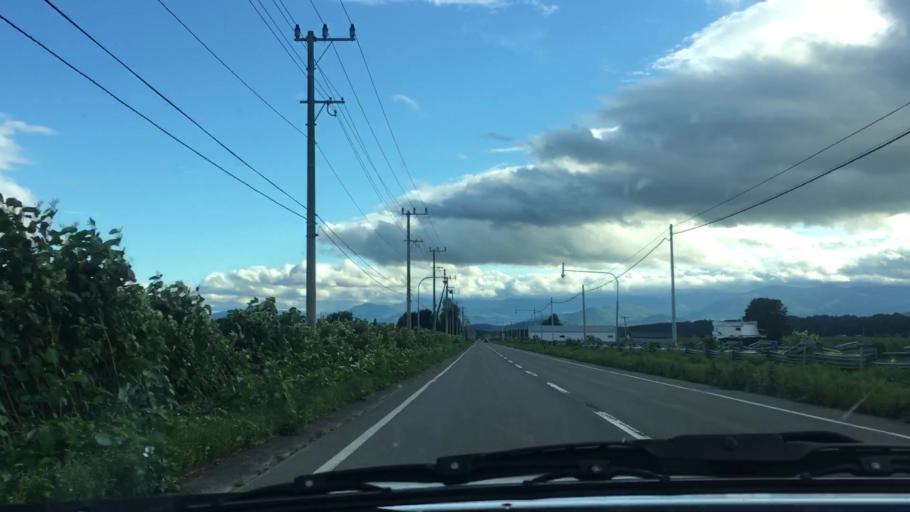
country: JP
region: Hokkaido
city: Otofuke
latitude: 43.1564
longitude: 142.9025
